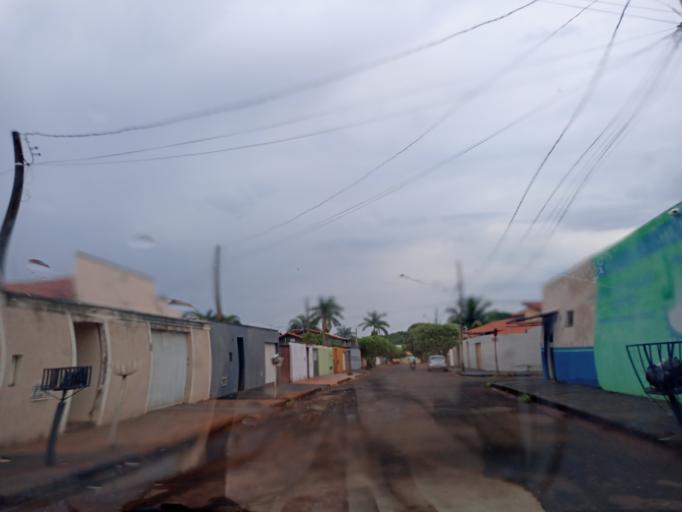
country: BR
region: Minas Gerais
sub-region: Ituiutaba
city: Ituiutaba
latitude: -18.9806
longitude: -49.4860
